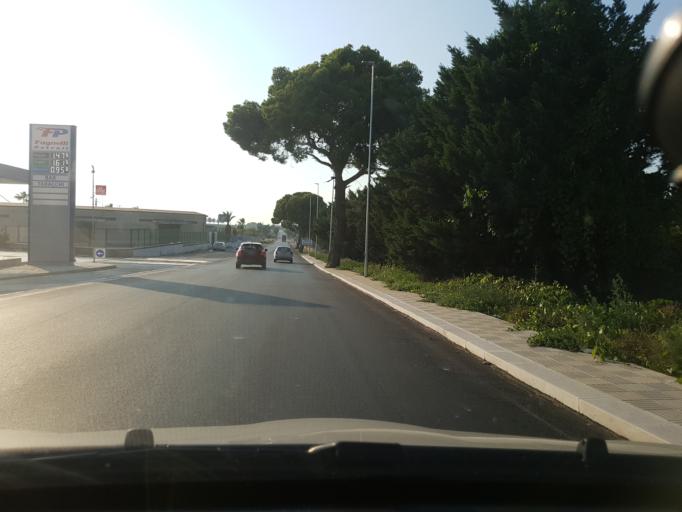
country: IT
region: Apulia
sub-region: Provincia di Foggia
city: Cerignola
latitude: 41.2677
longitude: 15.8846
